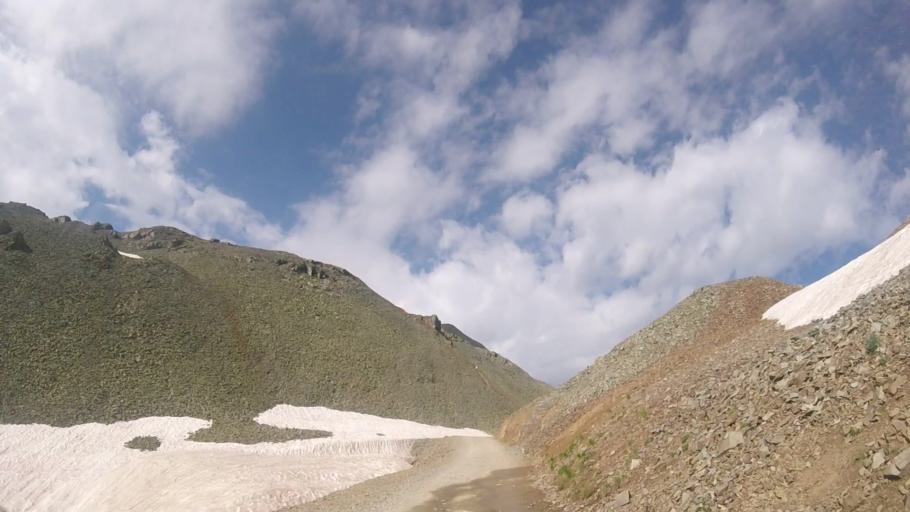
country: US
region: Colorado
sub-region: San Miguel County
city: Telluride
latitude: 37.8511
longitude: -107.7781
